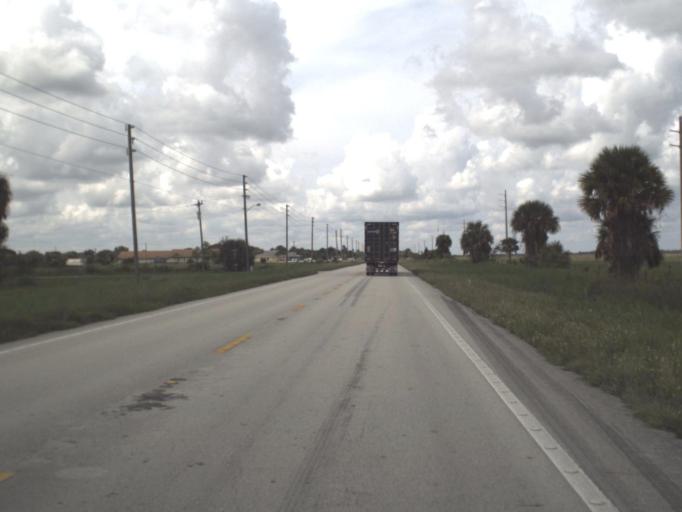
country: US
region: Florida
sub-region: Okeechobee County
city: Okeechobee
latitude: 27.2436
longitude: -80.9079
